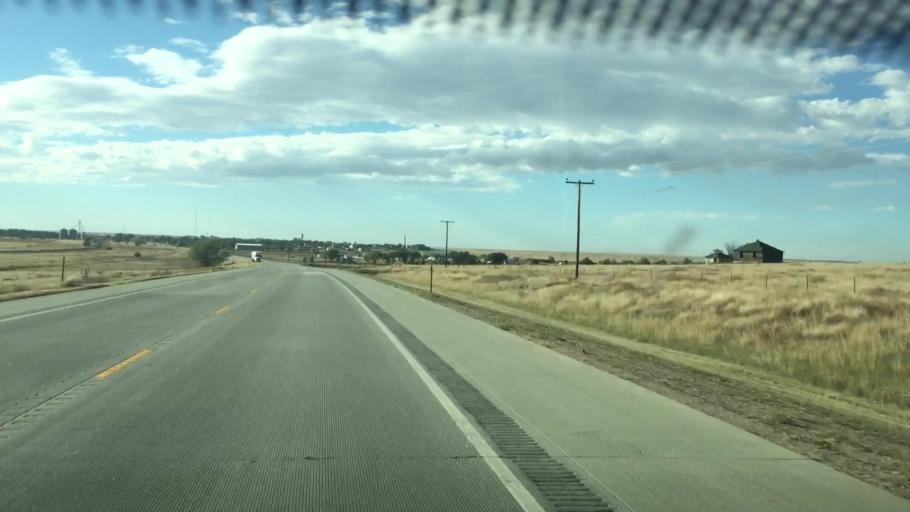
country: US
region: Colorado
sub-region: Lincoln County
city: Hugo
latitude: 39.1255
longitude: -103.4454
